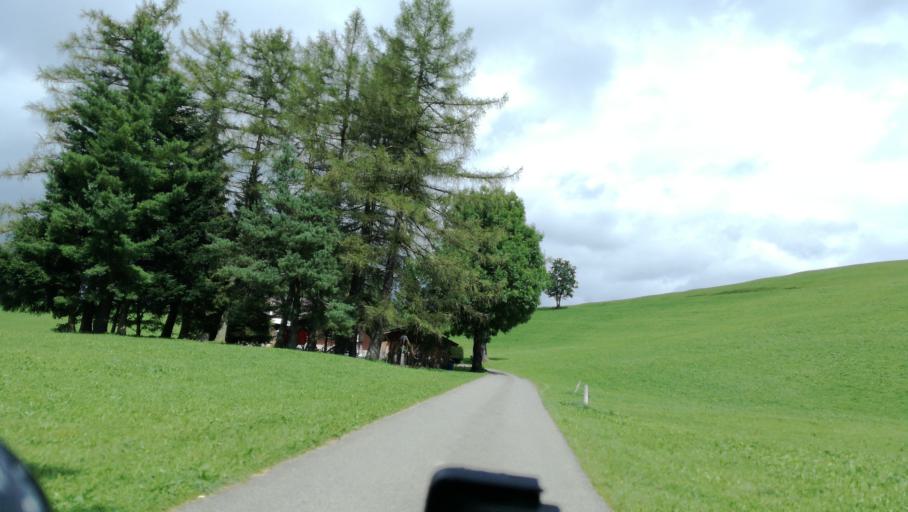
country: CH
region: Zug
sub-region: Zug
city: Walchwil
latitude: 47.1093
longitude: 8.5463
